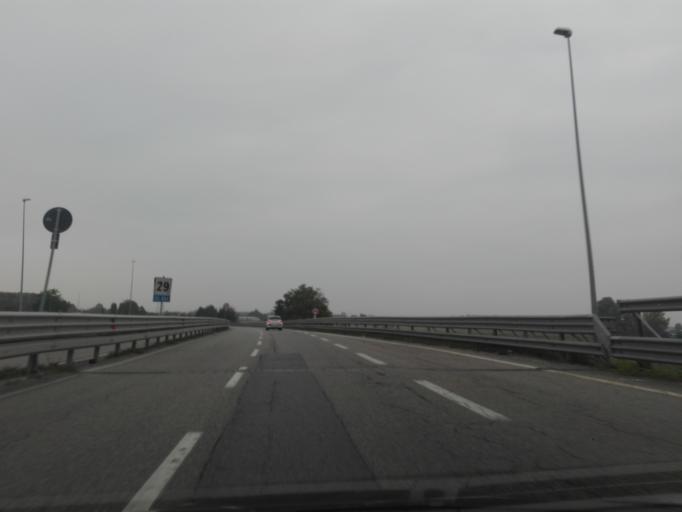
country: IT
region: Veneto
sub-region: Provincia di Verona
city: San Pietro di Morubio
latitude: 45.2476
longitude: 11.2383
